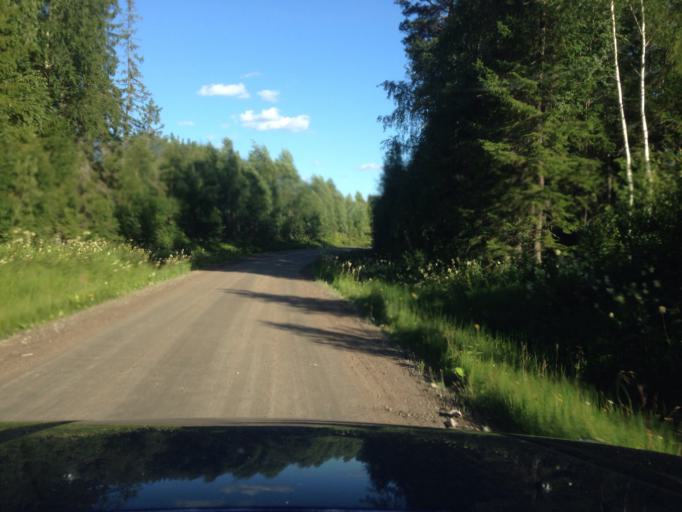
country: SE
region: Dalarna
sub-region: Ludvika Kommun
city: Abborrberget
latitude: 60.2298
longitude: 14.8389
